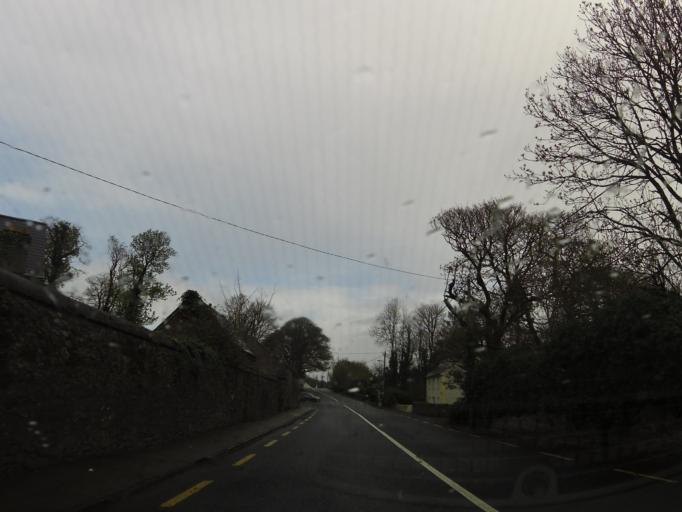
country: IE
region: Connaught
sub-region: Sligo
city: Collooney
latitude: 54.1879
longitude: -8.4921
